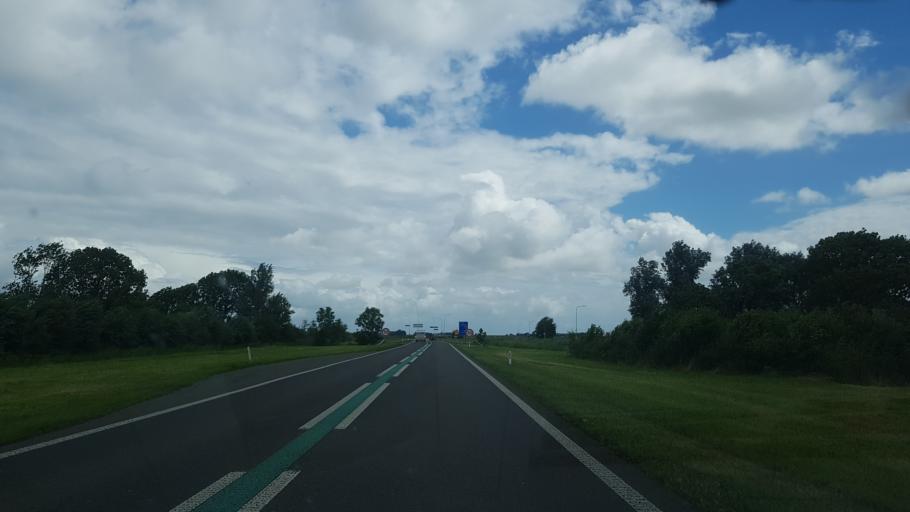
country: NL
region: Friesland
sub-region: Gemeente Dongeradeel
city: Anjum
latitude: 53.3681
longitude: 6.0887
